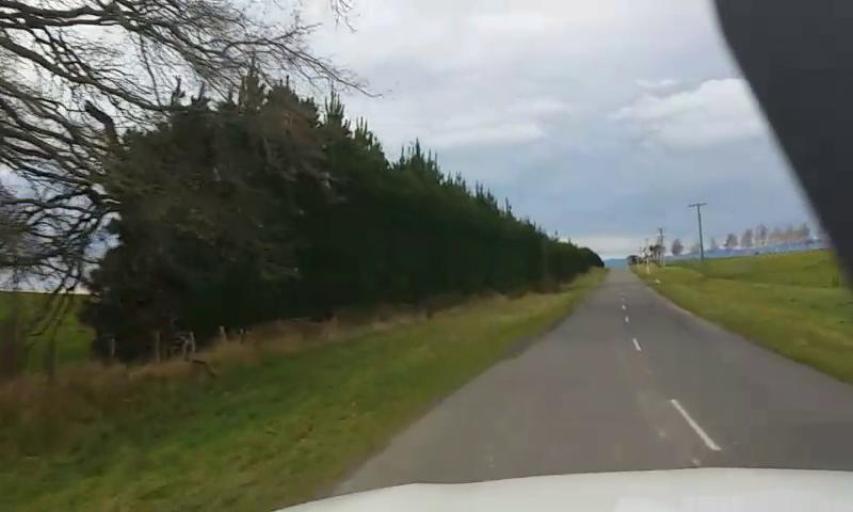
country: NZ
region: Canterbury
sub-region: Waimakariri District
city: Kaiapoi
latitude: -43.2910
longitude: 172.4700
